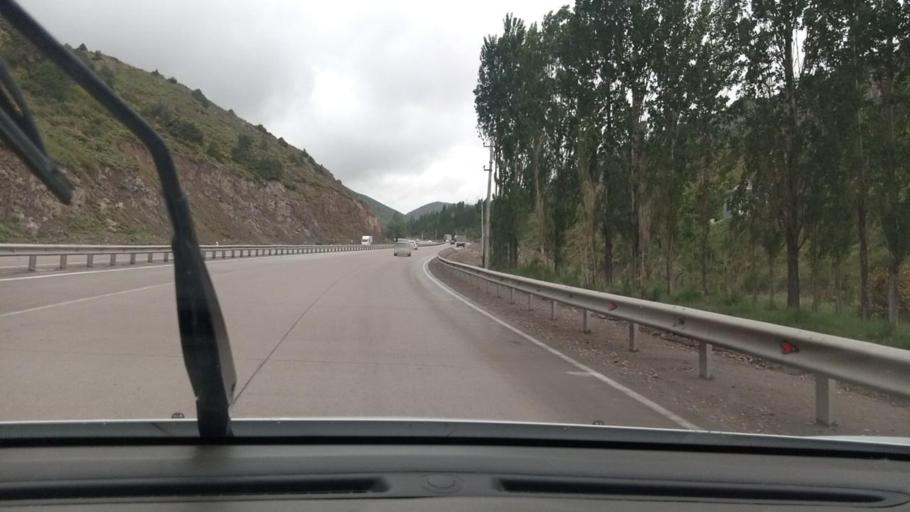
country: UZ
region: Toshkent
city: Angren
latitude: 41.0417
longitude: 70.5760
